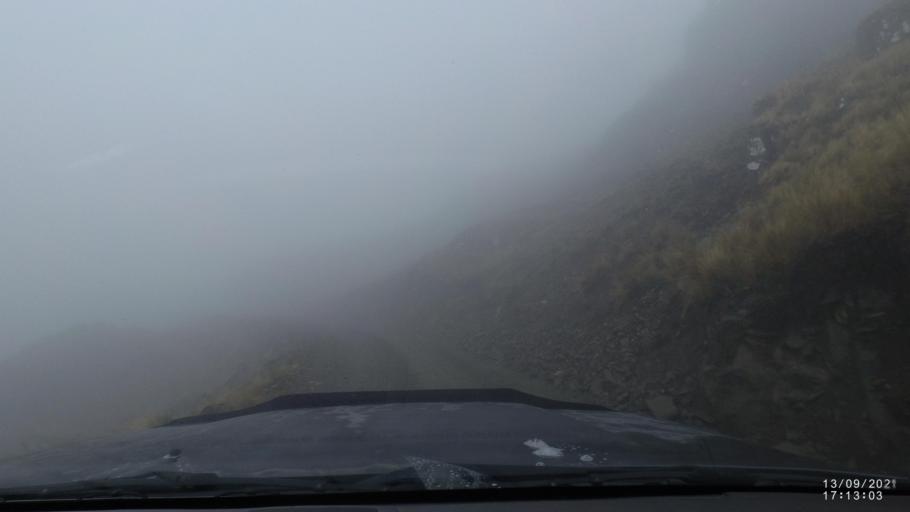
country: BO
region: Cochabamba
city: Colomi
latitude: -17.3392
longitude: -65.7484
